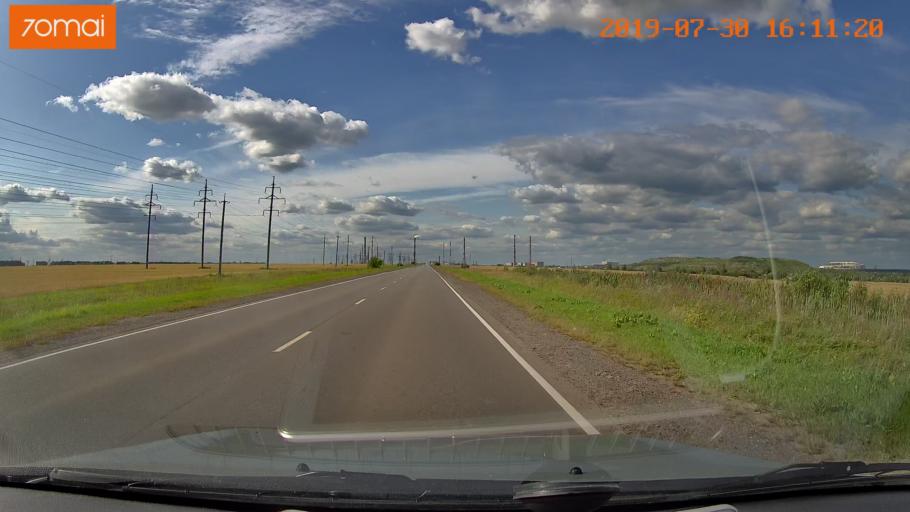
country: RU
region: Moskovskaya
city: Lopatinskiy
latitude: 55.2744
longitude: 38.7119
